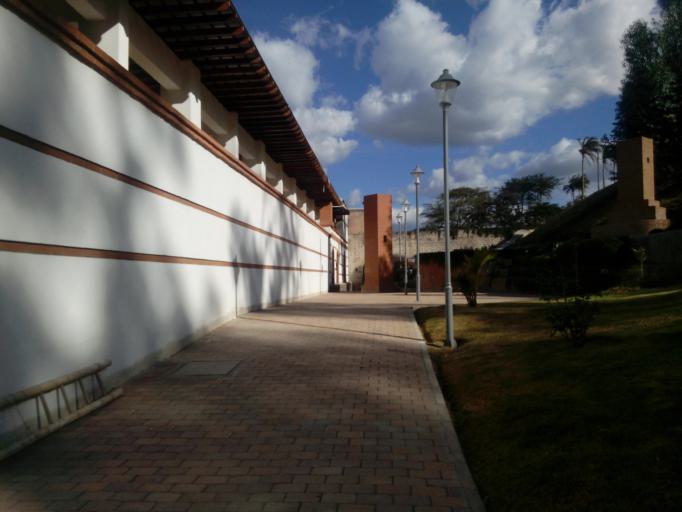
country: EC
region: Imbabura
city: Ibarra
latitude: 0.4053
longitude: -78.1748
